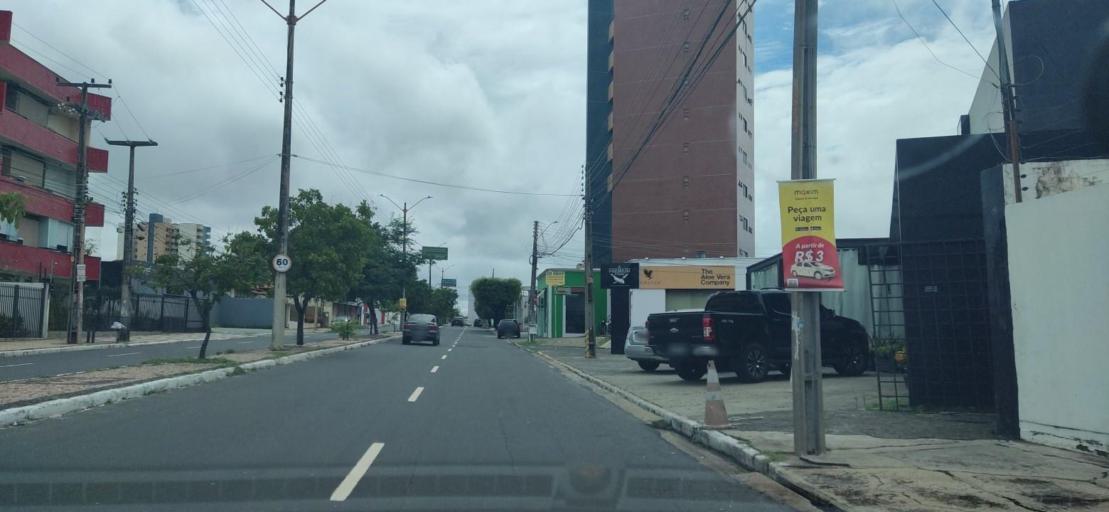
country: BR
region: Piaui
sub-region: Teresina
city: Teresina
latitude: -5.0728
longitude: -42.7772
